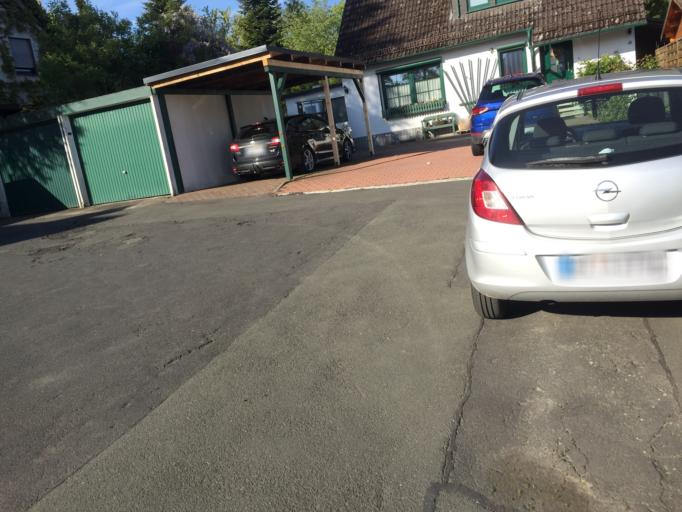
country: DE
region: Hesse
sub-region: Regierungsbezirk Giessen
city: Wetzlar
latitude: 50.5418
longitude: 8.5339
